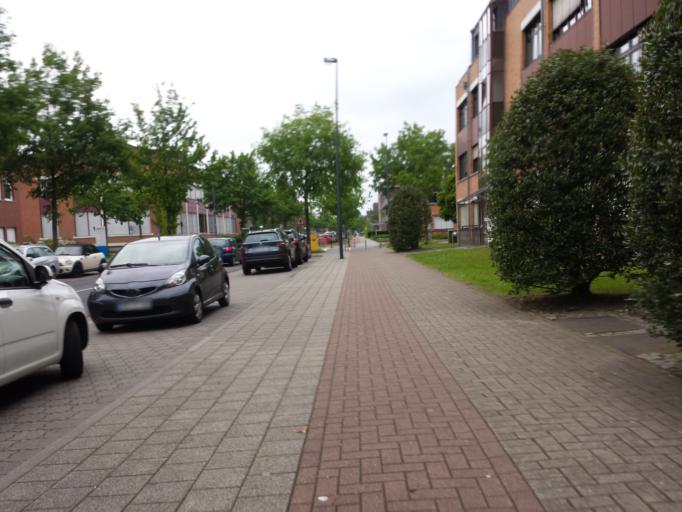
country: DE
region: Bremen
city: Bremen
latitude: 53.1074
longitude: 8.8464
